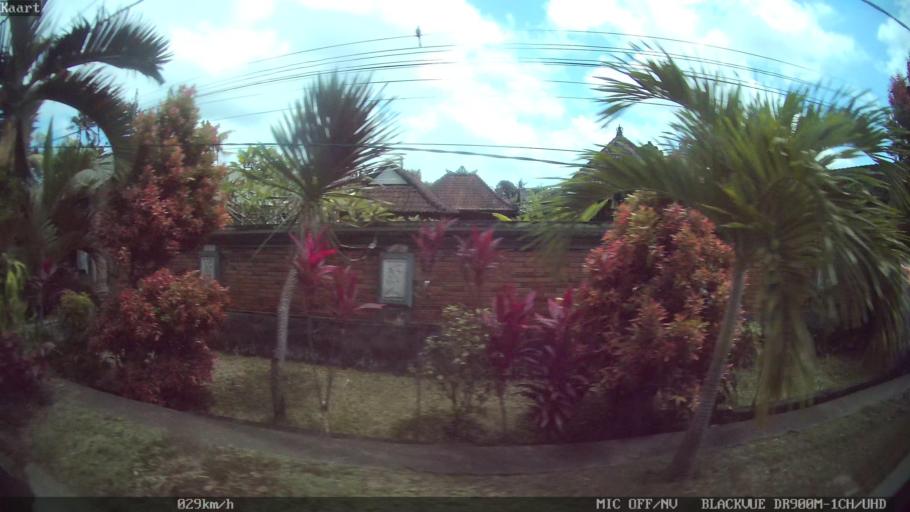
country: ID
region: Bali
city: Banjar Tebongkang
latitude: -8.5539
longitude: 115.2841
